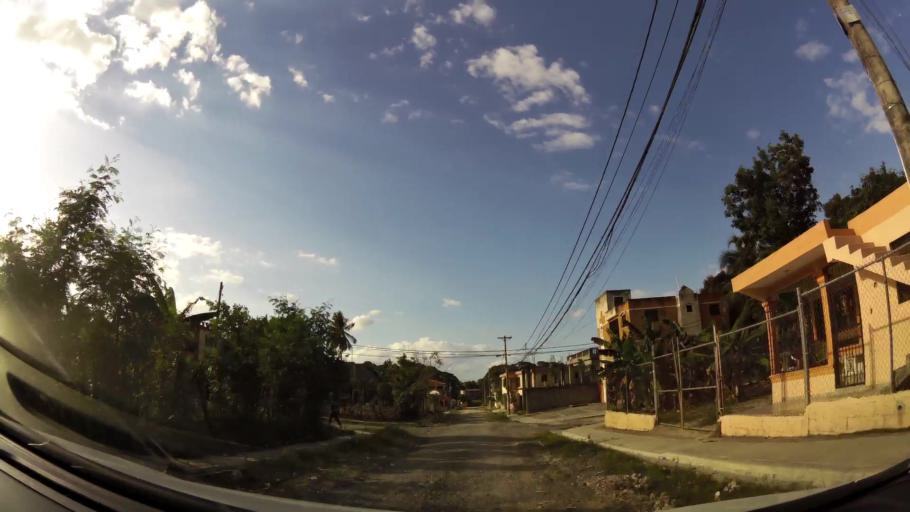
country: DO
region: Nacional
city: Ensanche Luperon
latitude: 18.5588
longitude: -69.8943
